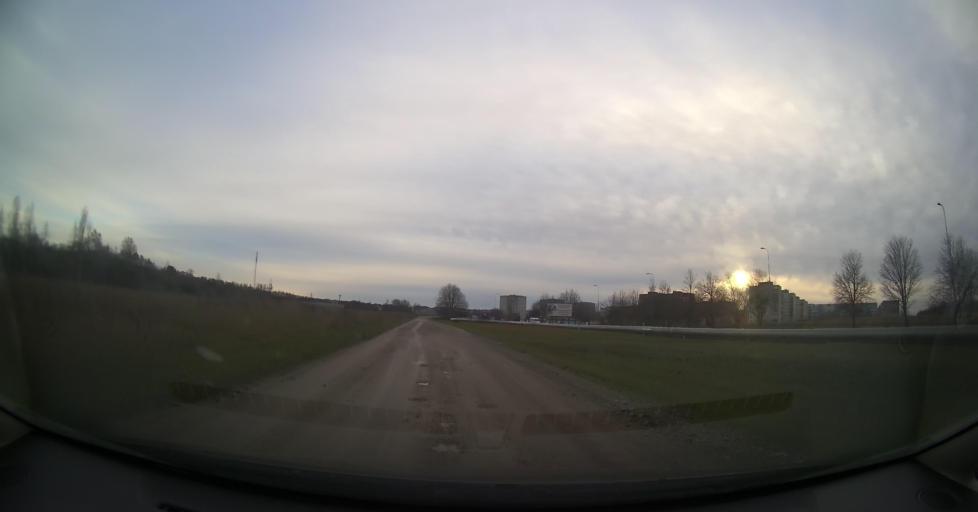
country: EE
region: Ida-Virumaa
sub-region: Johvi vald
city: Johvi
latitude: 59.3415
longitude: 27.4205
